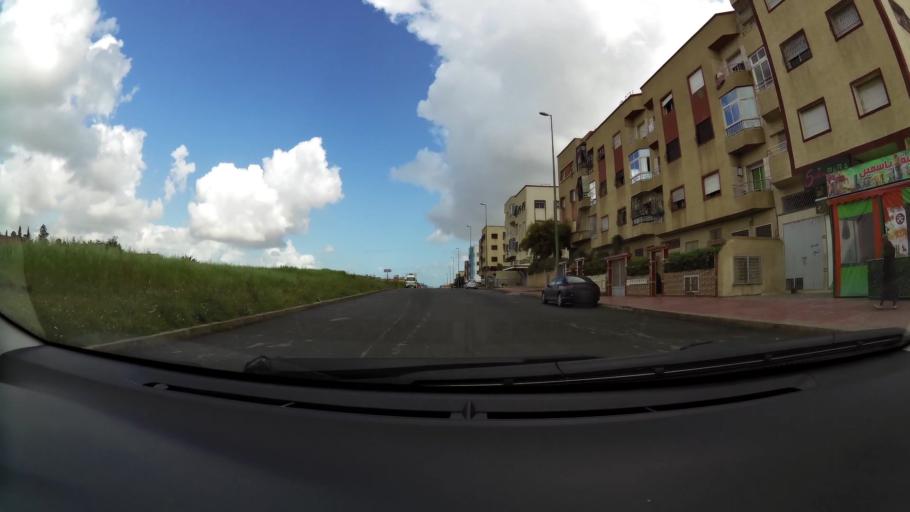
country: MA
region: Grand Casablanca
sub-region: Mediouna
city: Tit Mellil
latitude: 33.5442
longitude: -7.4839
